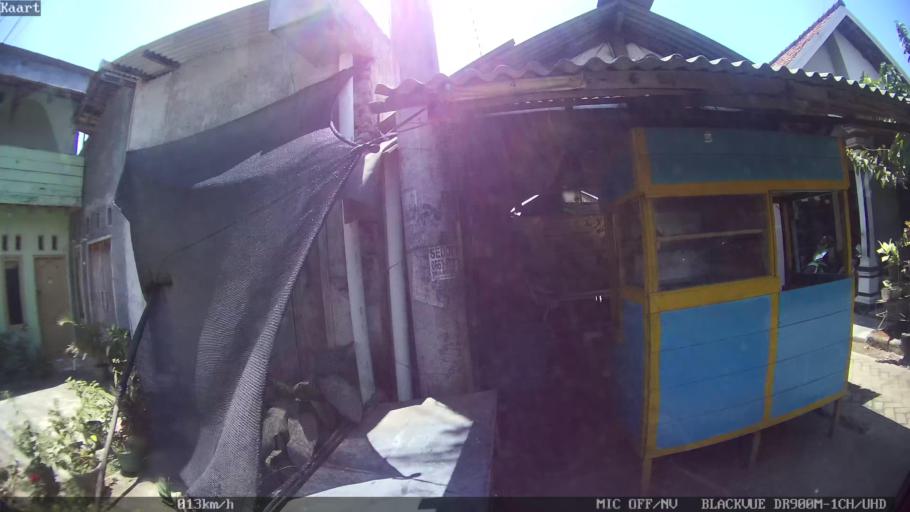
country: ID
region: Lampung
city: Kedaton
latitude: -5.3754
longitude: 105.2838
